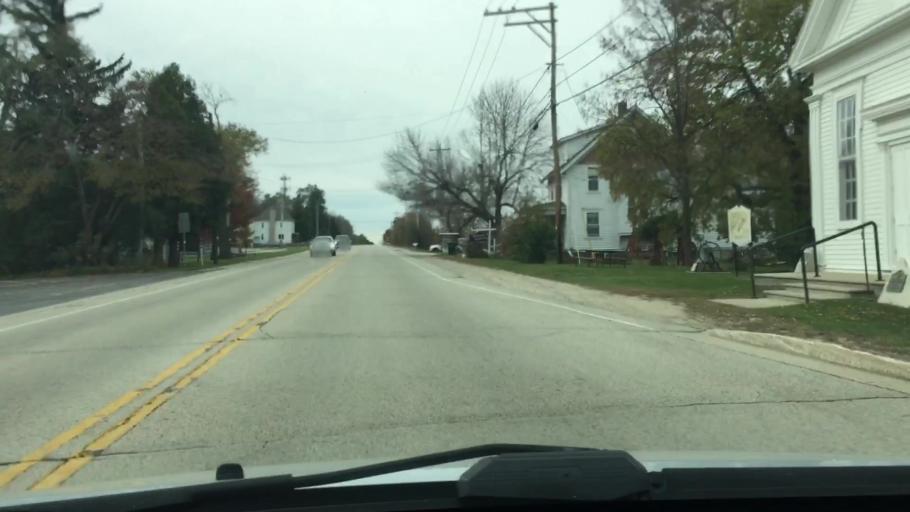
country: US
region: Wisconsin
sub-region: Waukesha County
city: Muskego
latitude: 42.9443
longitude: -88.1601
